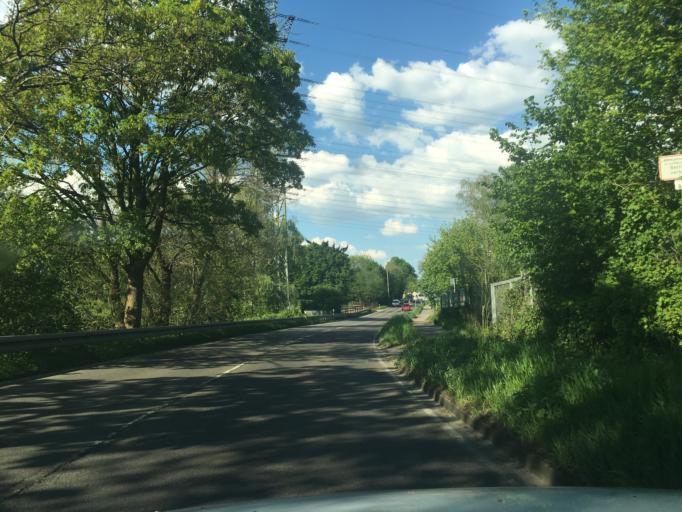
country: DE
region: North Rhine-Westphalia
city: Haan
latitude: 51.1731
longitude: 6.9853
